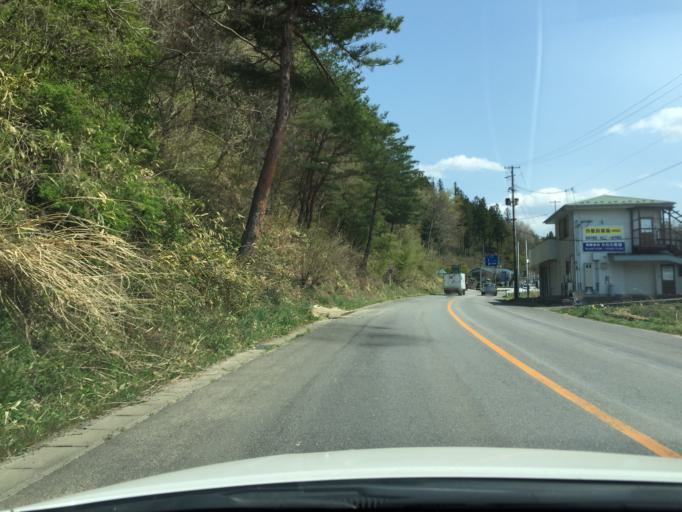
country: JP
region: Fukushima
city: Namie
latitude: 37.4380
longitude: 140.7978
